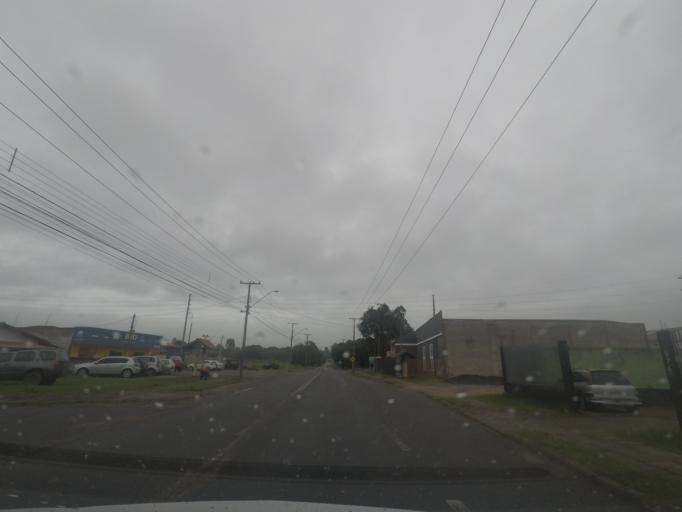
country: BR
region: Parana
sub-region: Quatro Barras
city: Quatro Barras
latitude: -25.3706
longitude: -49.0839
